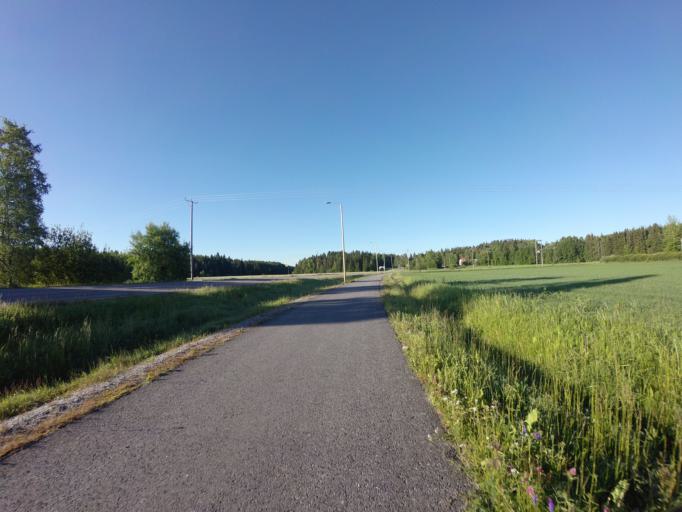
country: FI
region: Varsinais-Suomi
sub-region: Turku
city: Vahto
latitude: 60.5264
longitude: 22.3481
